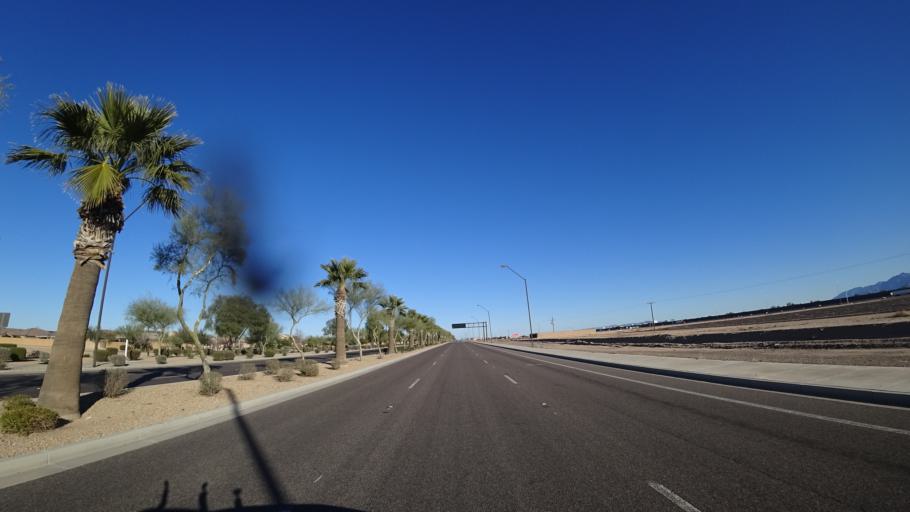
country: US
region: Arizona
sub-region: Maricopa County
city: Litchfield Park
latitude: 33.4648
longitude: -112.4079
